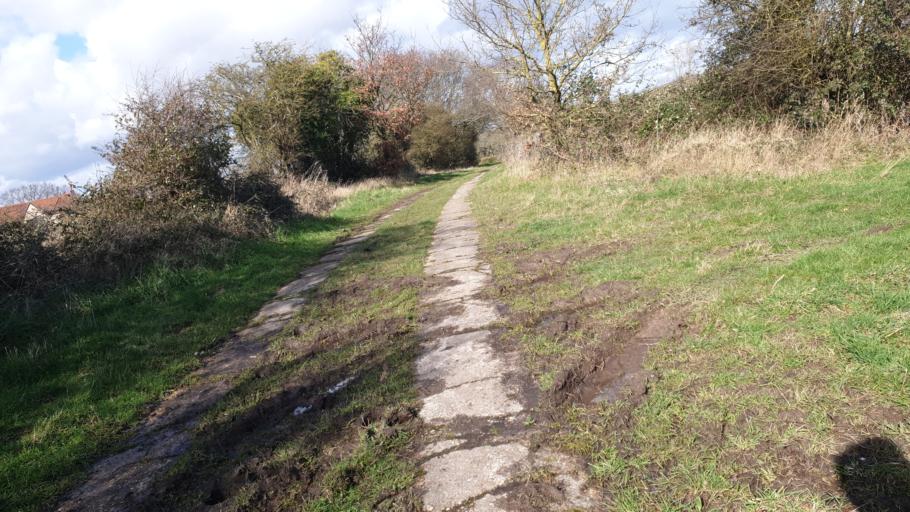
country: GB
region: England
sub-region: Essex
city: Little Clacton
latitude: 51.8434
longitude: 1.1632
